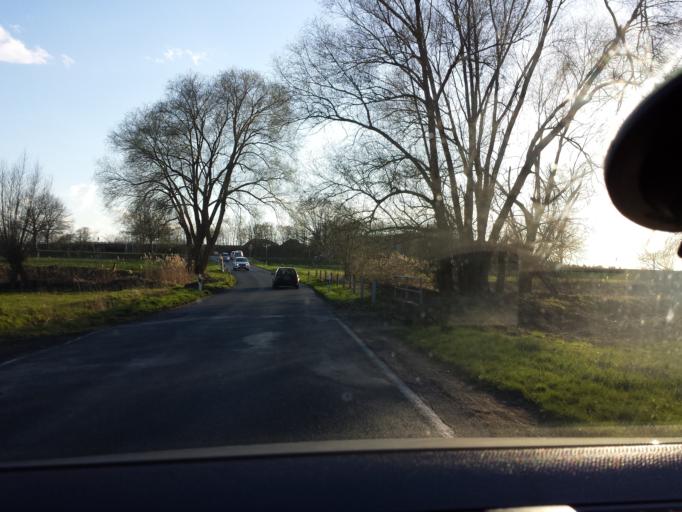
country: DE
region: Lower Saxony
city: Braunschweig
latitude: 52.2997
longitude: 10.4825
